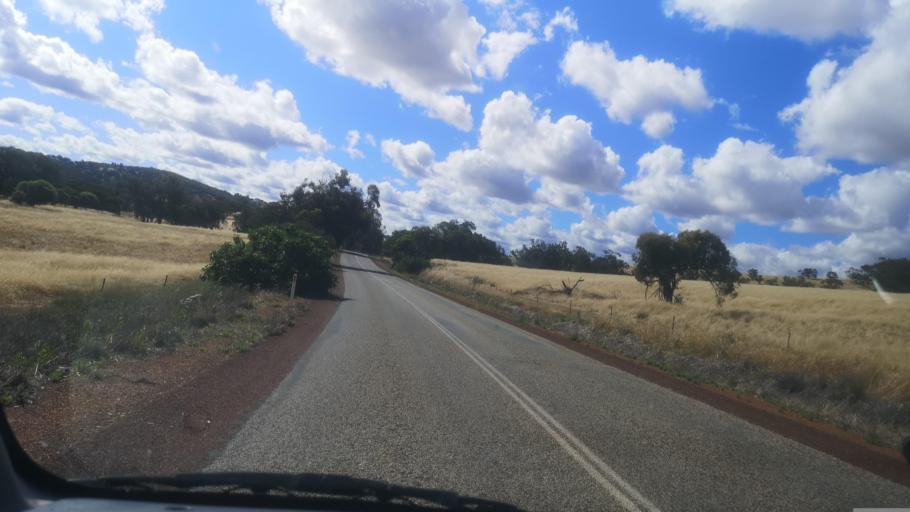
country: AU
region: Western Australia
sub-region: Toodyay
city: Toodyay
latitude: -31.5011
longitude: 116.4459
